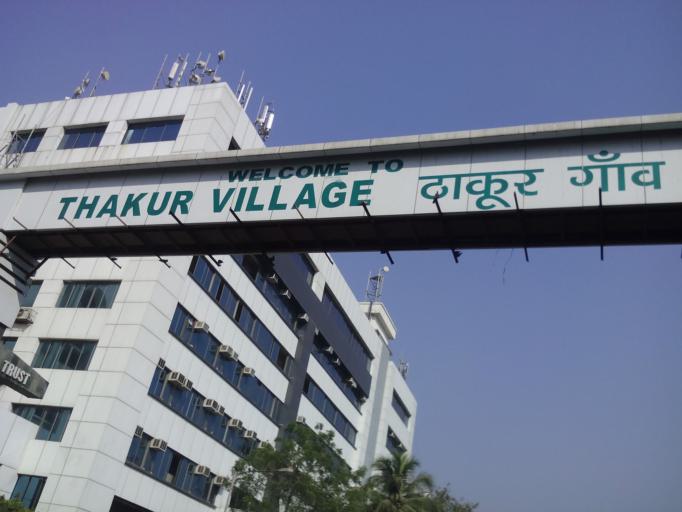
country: IN
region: Maharashtra
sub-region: Mumbai Suburban
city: Borivli
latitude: 19.2062
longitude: 72.8726
